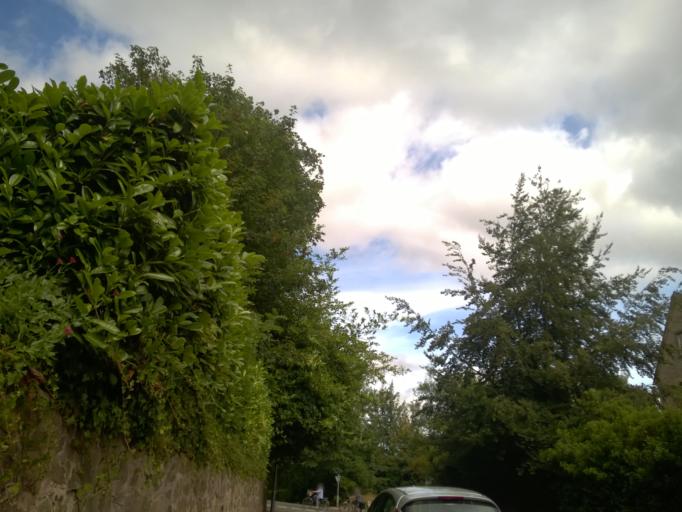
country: GB
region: England
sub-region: Worcestershire
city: Great Malvern
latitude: 52.1116
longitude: -2.3225
